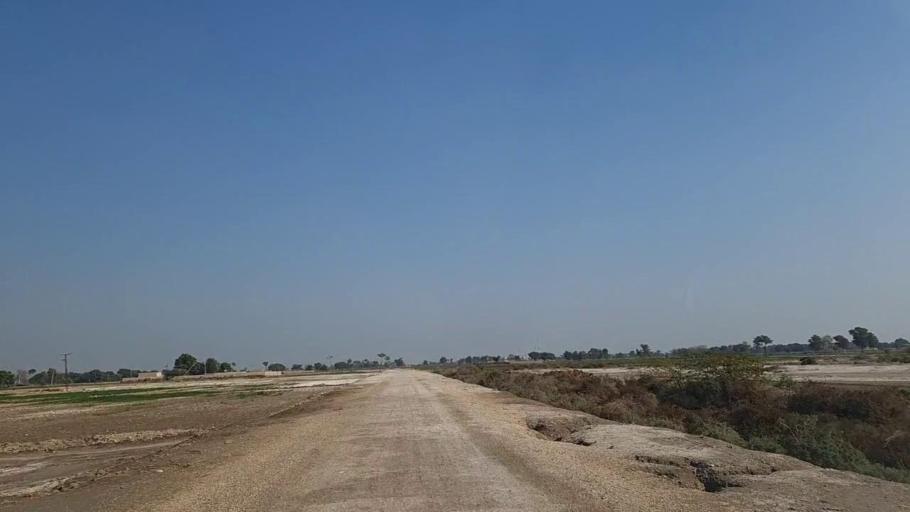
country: PK
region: Sindh
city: Daur
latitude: 26.3570
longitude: 68.3429
